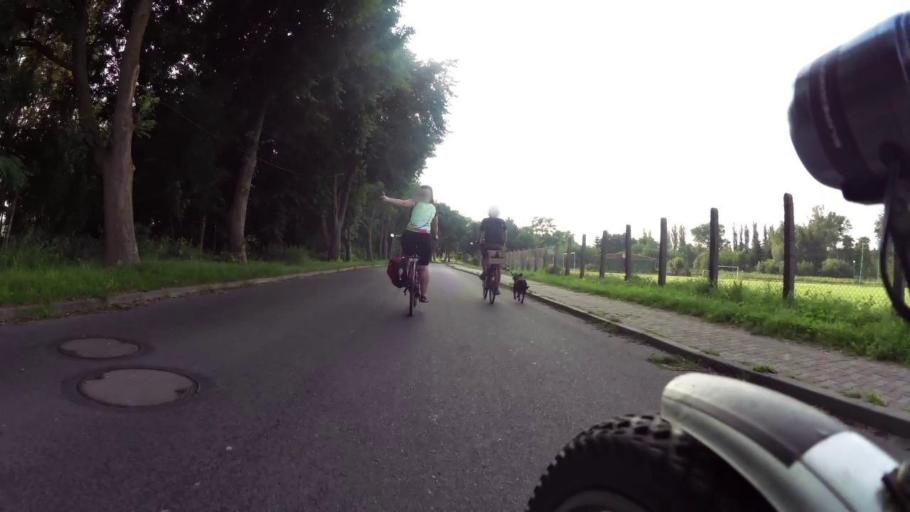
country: PL
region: West Pomeranian Voivodeship
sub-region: Powiat goleniowski
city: Stepnica
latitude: 53.6620
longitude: 14.5103
